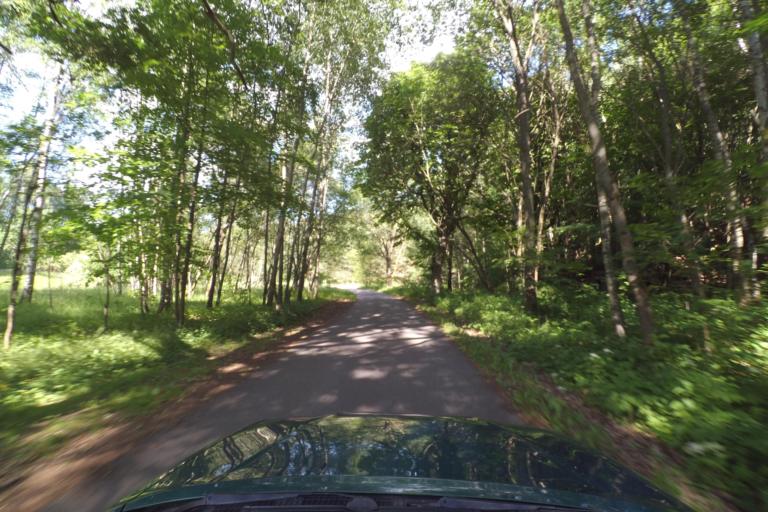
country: CZ
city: Osecna
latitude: 50.6737
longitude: 14.8874
